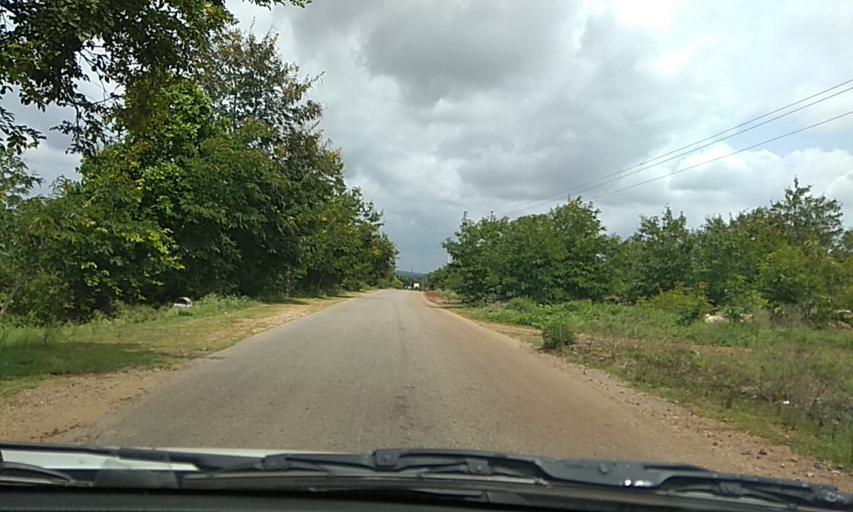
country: IN
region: Karnataka
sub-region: Chamrajnagar
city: Gundlupet
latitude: 11.7970
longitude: 76.7967
